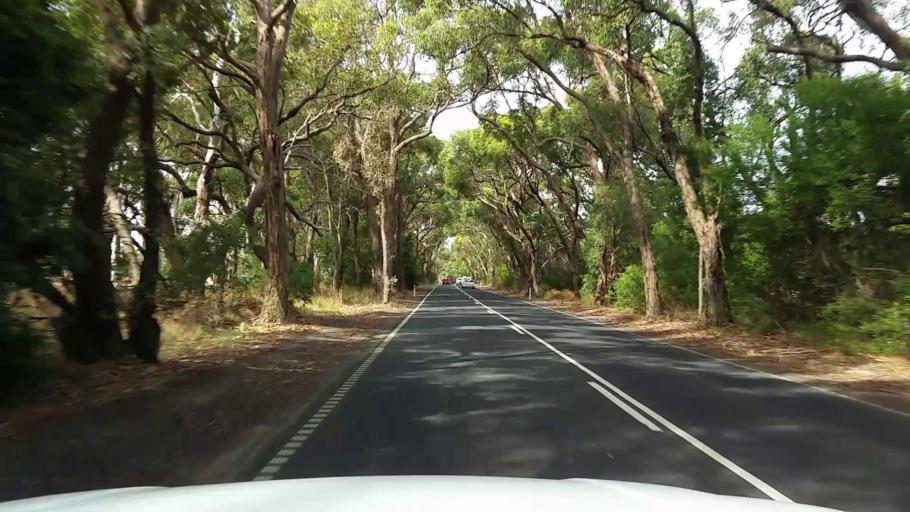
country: AU
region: Victoria
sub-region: Mornington Peninsula
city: Mount Martha
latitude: -38.2987
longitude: 145.0787
